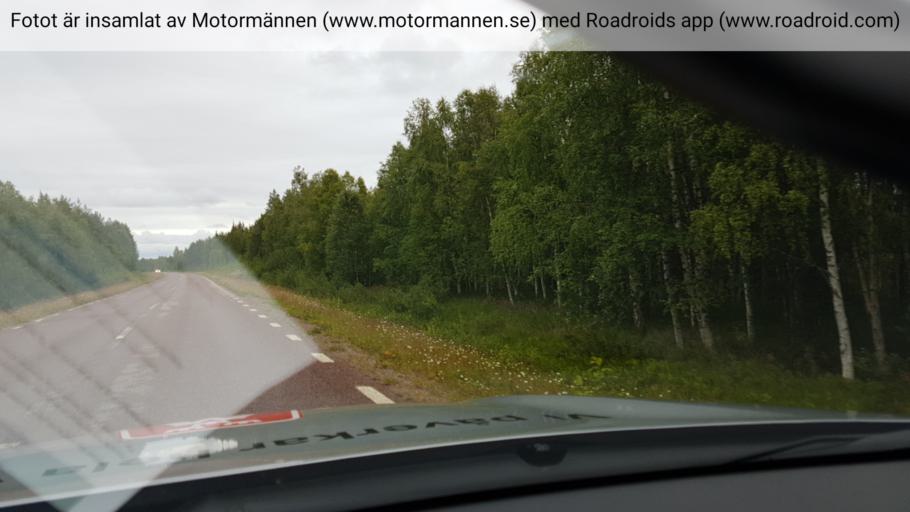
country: SE
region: Norrbotten
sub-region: Pajala Kommun
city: Pajala
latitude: 67.1440
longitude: 22.6196
